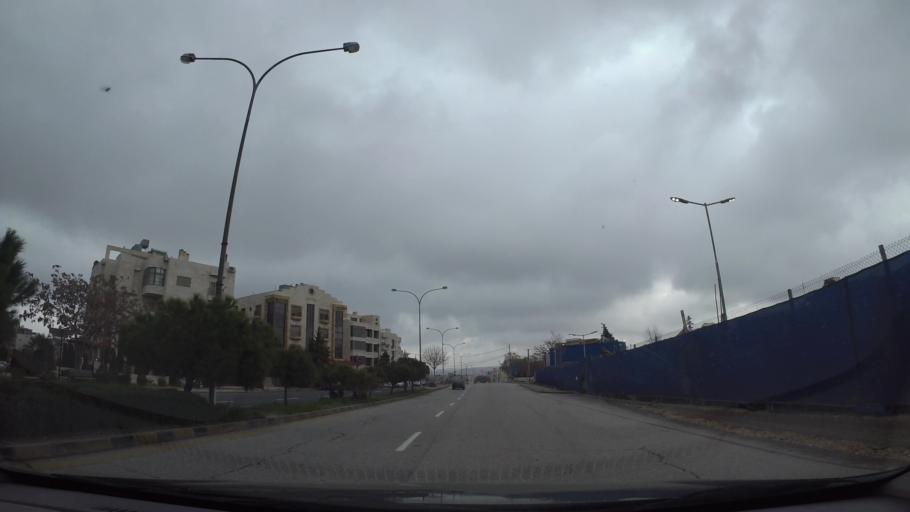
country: JO
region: Amman
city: Al Bunayyat ash Shamaliyah
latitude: 31.9468
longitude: 35.8800
